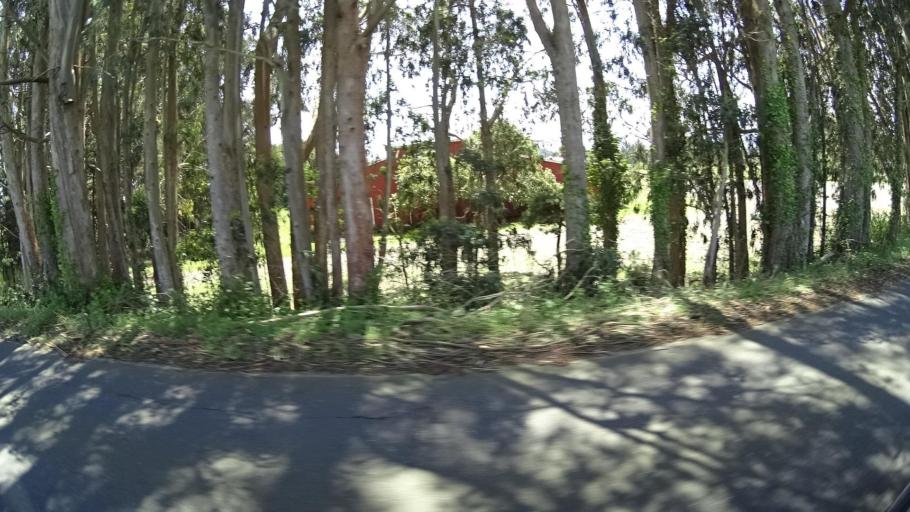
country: US
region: California
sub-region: Humboldt County
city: Fortuna
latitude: 40.6442
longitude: -124.2160
